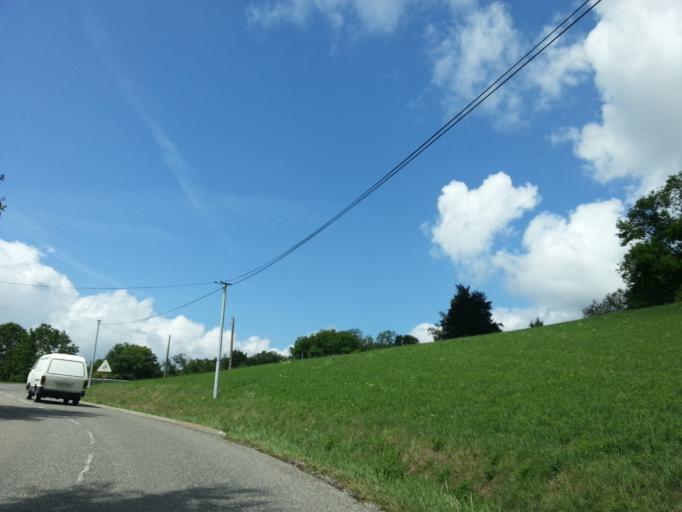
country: FR
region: Rhone-Alpes
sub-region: Departement de la Haute-Savoie
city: Talloires
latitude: 45.8534
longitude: 6.2148
